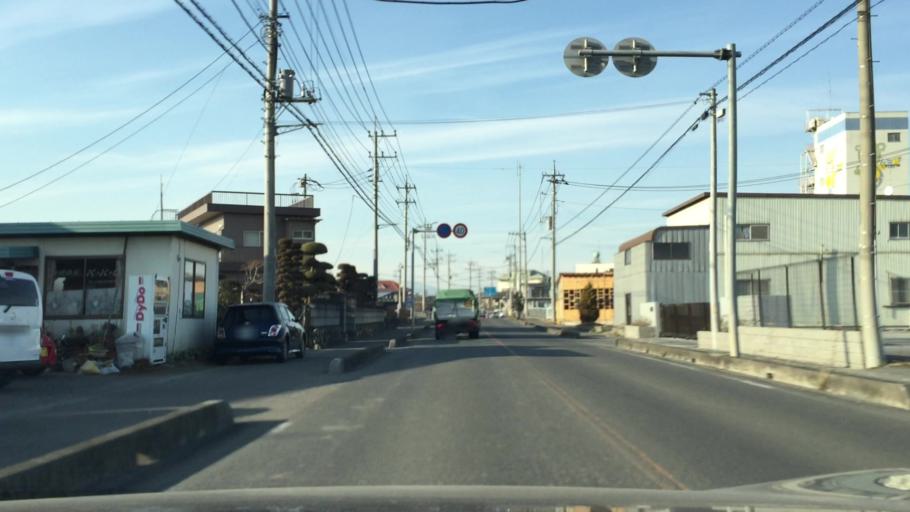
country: JP
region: Saitama
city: Menuma
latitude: 36.1999
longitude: 139.3750
